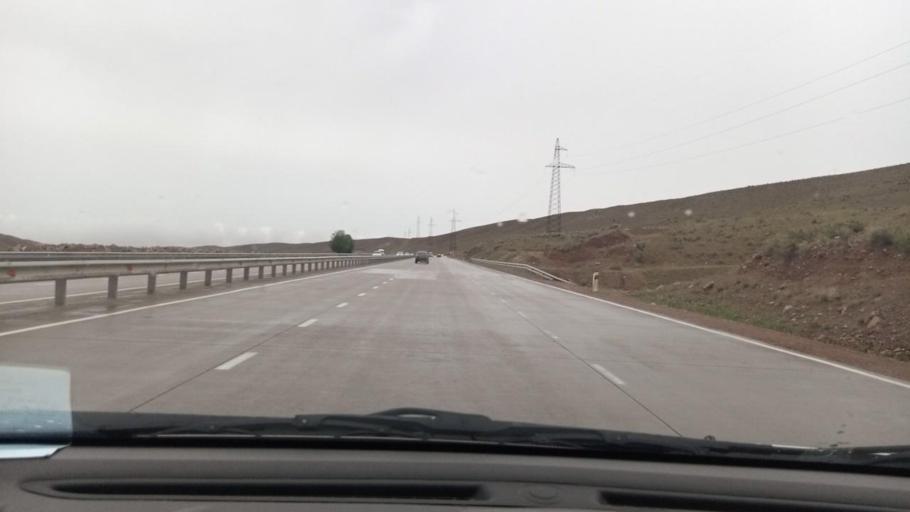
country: UZ
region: Namangan
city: Pop Shahri
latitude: 40.9389
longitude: 70.6922
